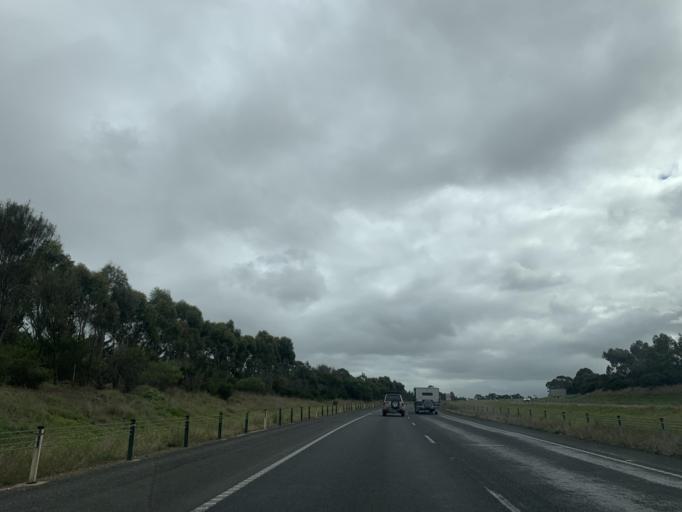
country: AU
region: Victoria
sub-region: Moorabool
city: Bacchus Marsh
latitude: -37.6326
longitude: 144.3506
